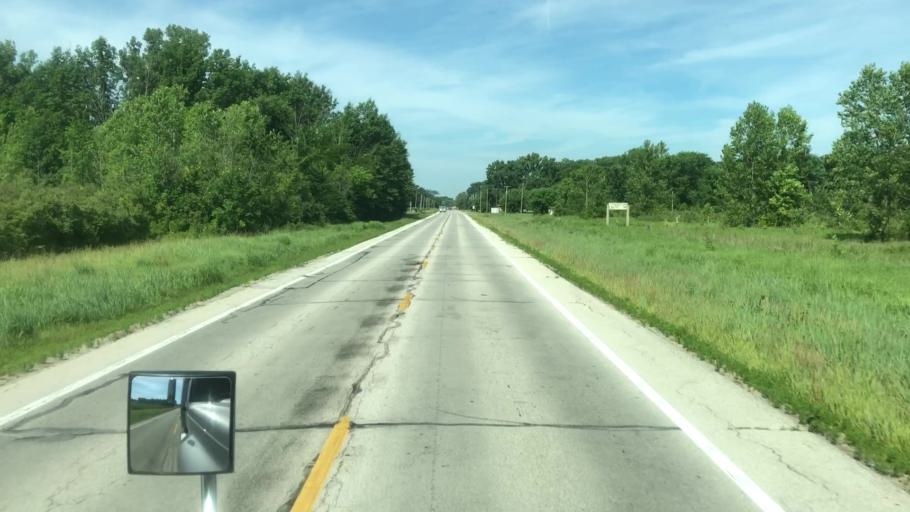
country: US
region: Ohio
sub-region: Ottawa County
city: Port Clinton
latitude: 41.4090
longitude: -82.9606
